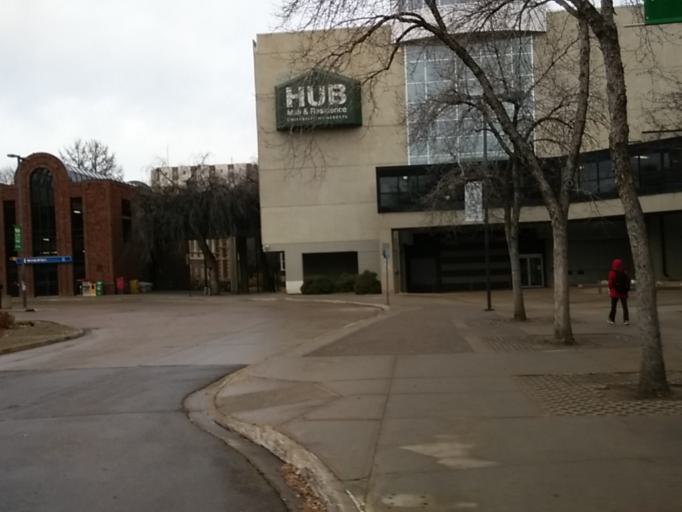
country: CA
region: Alberta
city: Edmonton
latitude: 53.5245
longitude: -113.5208
